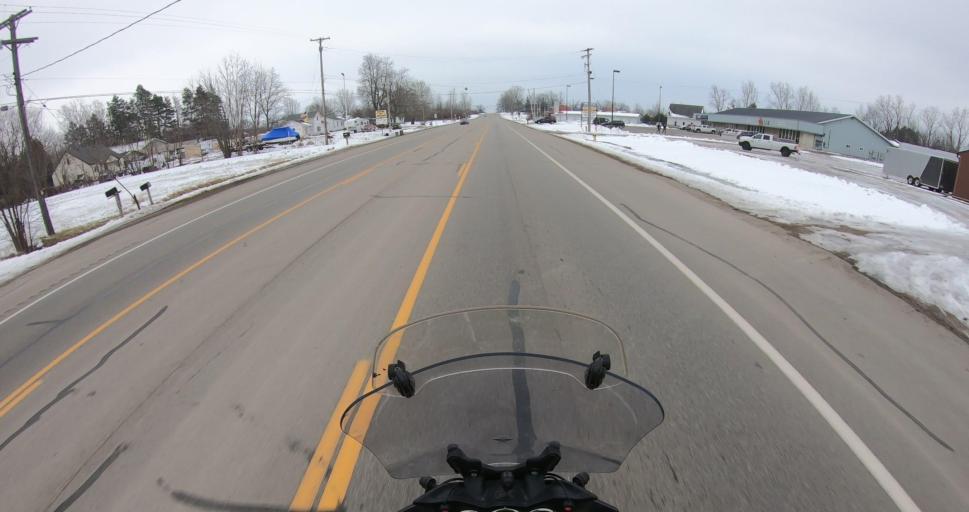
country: US
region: Michigan
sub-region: Genesee County
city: Clio
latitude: 43.1723
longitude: -83.7099
